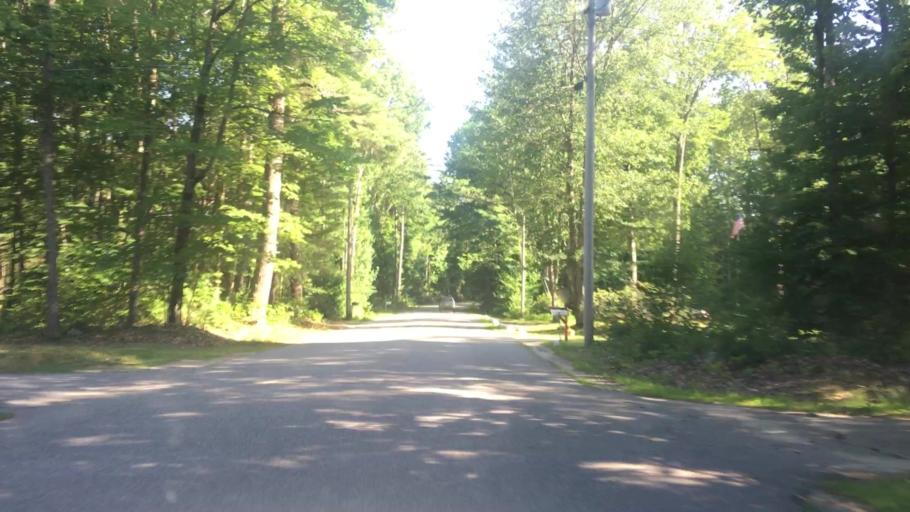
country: US
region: Maine
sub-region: Cumberland County
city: Gorham
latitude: 43.7209
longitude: -70.5152
